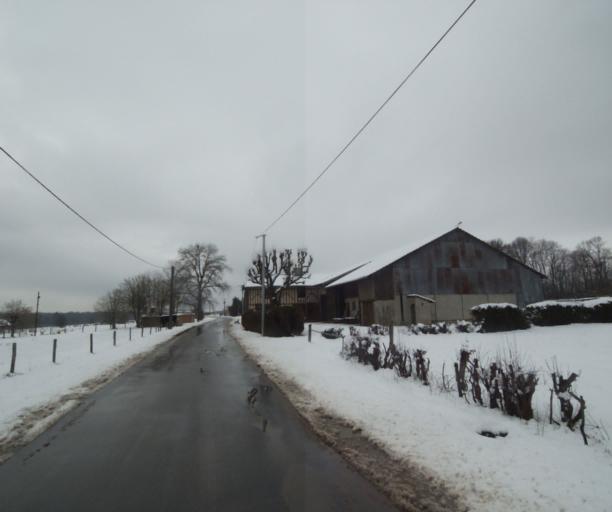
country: FR
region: Champagne-Ardenne
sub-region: Departement de la Haute-Marne
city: Laneuville-a-Remy
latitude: 48.4757
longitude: 4.8863
